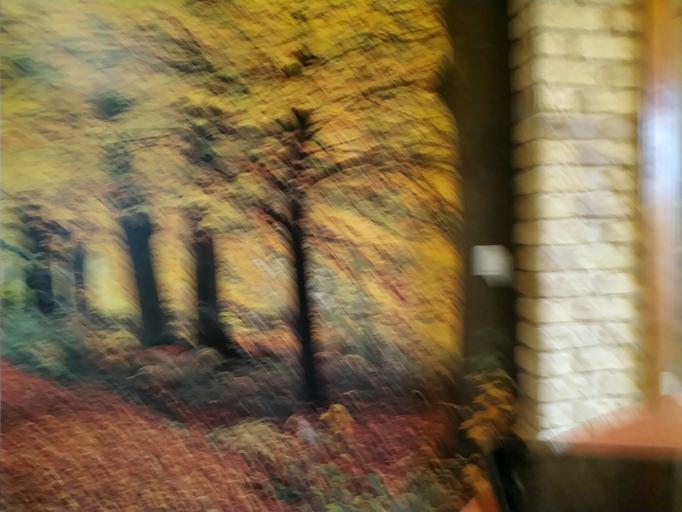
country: RU
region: Vologda
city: Nelazskoye
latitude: 59.3837
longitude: 37.6100
